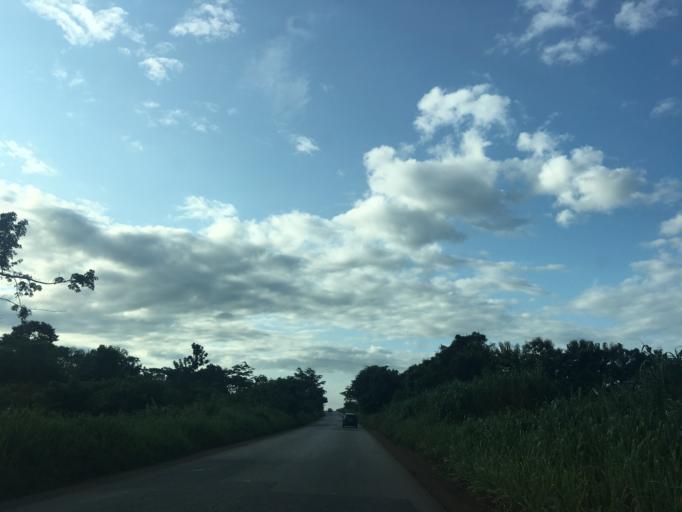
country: GH
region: Western
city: Bibiani
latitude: 6.3119
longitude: -2.2507
